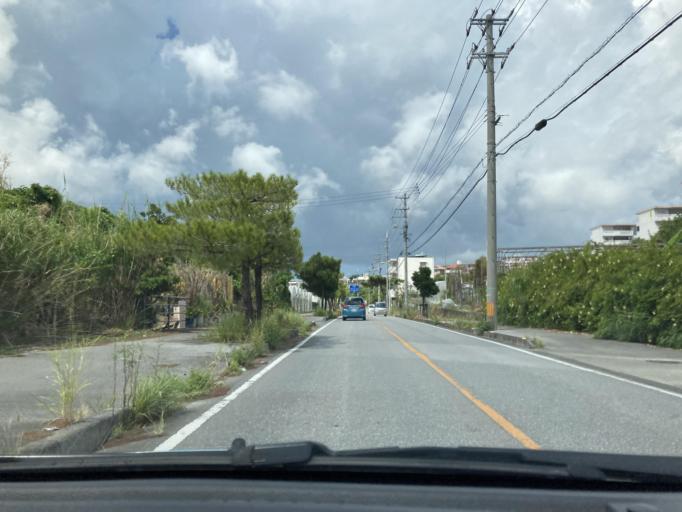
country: JP
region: Okinawa
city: Tomigusuku
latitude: 26.1736
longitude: 127.7521
